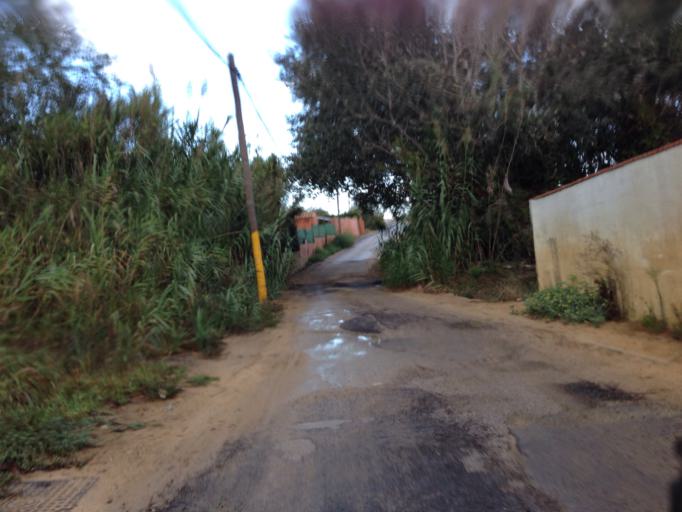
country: ES
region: Andalusia
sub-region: Provincia de Cadiz
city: Conil de la Frontera
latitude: 36.2975
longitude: -6.1104
